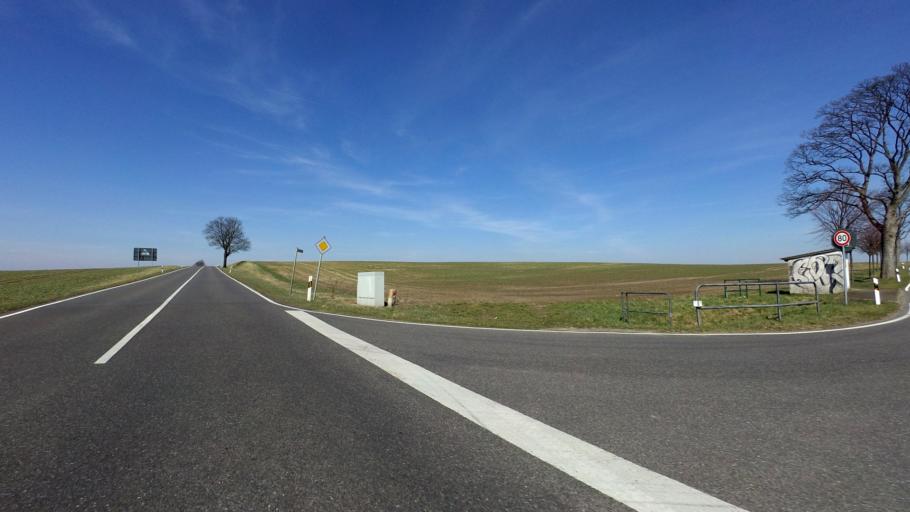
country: DE
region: Brandenburg
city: Protzel
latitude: 52.6050
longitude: 14.0231
